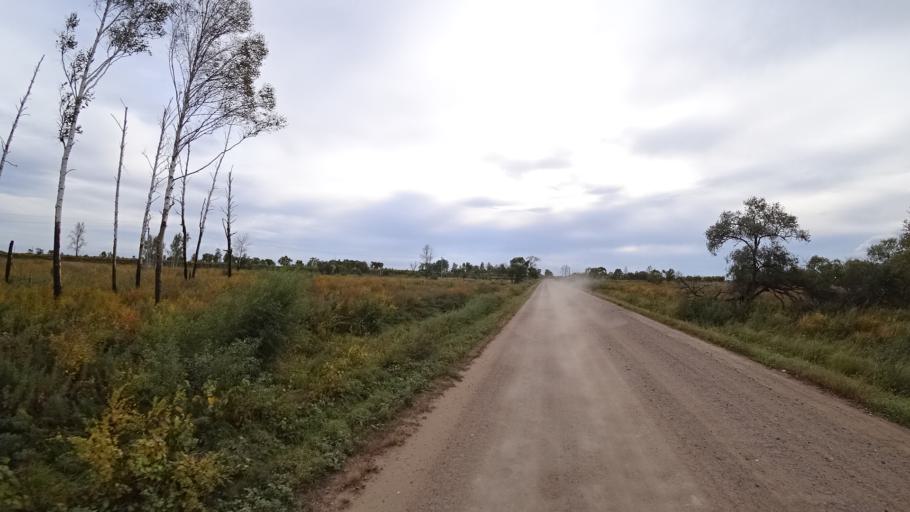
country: RU
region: Amur
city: Arkhara
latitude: 49.3778
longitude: 130.1749
